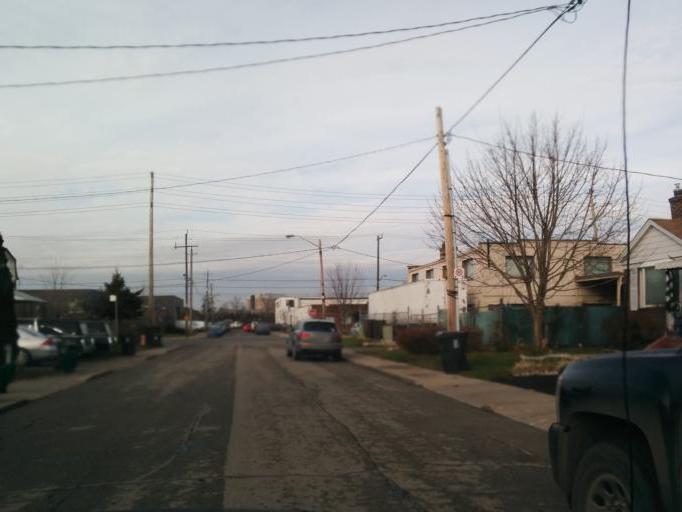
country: CA
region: Ontario
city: Etobicoke
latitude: 43.6011
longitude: -79.5137
